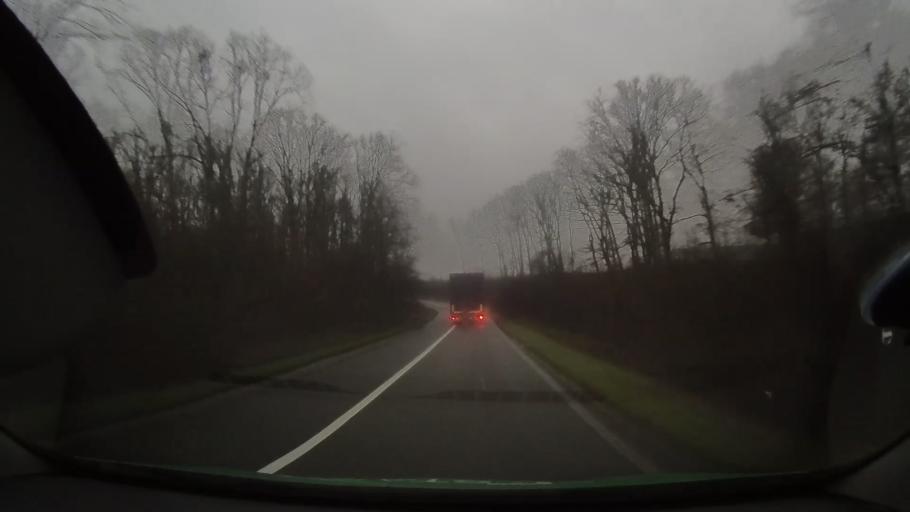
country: RO
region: Arad
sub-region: Comuna Beliu
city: Beliu
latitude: 46.5118
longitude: 21.9615
